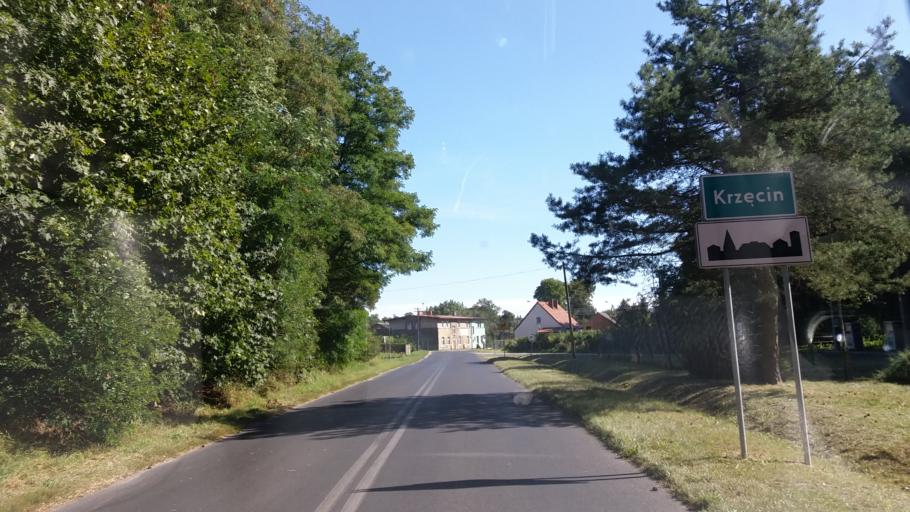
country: PL
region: West Pomeranian Voivodeship
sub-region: Powiat choszczenski
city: Krzecin
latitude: 53.0851
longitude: 15.4795
